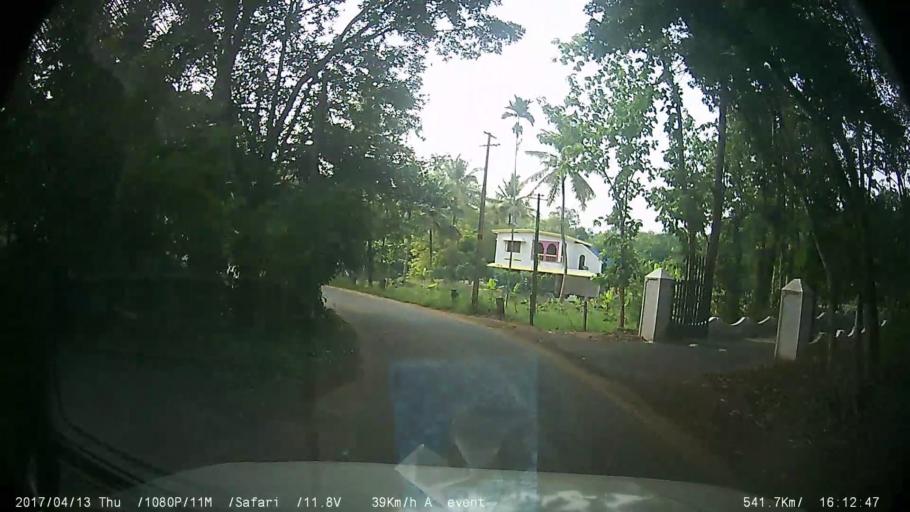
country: IN
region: Kerala
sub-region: Ernakulam
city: Piravam
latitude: 9.8201
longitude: 76.5156
